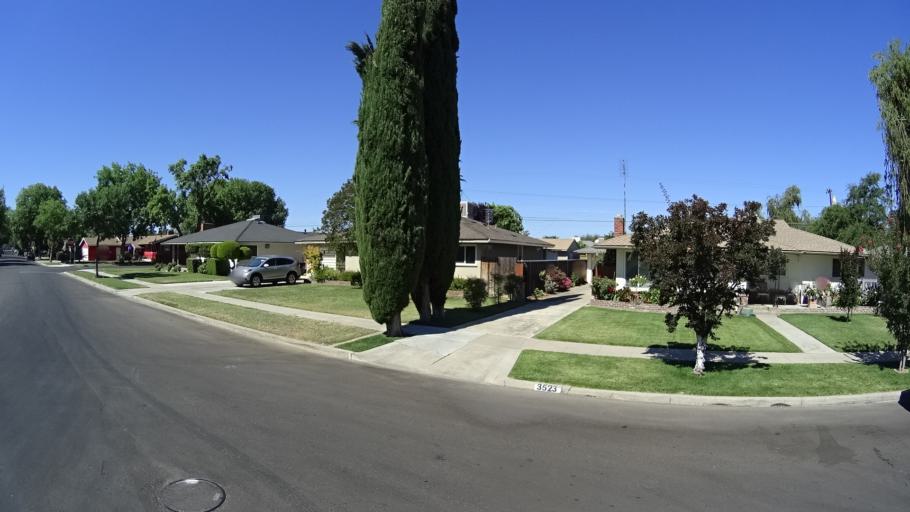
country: US
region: California
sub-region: Fresno County
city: Fresno
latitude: 36.7825
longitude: -119.8343
